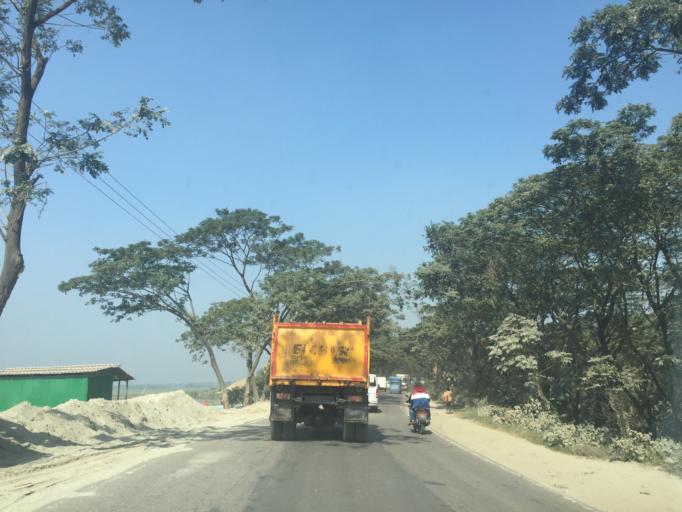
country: BD
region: Dhaka
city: Tungi
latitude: 23.8316
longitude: 90.3407
